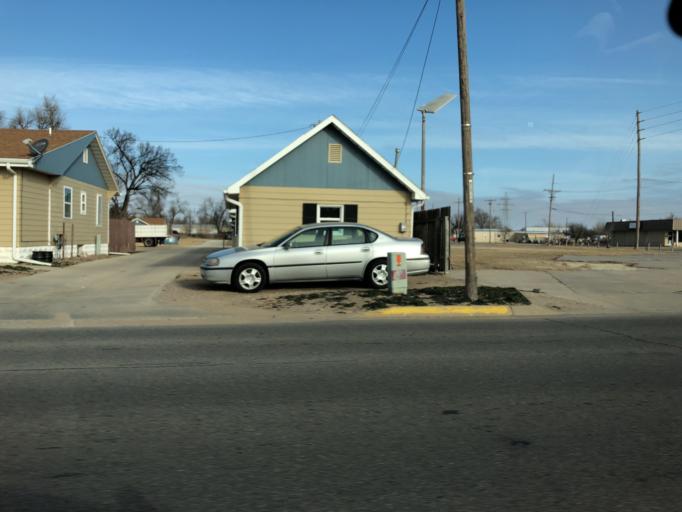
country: US
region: Kansas
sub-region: Reno County
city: Hutchinson
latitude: 38.0570
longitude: -97.9506
